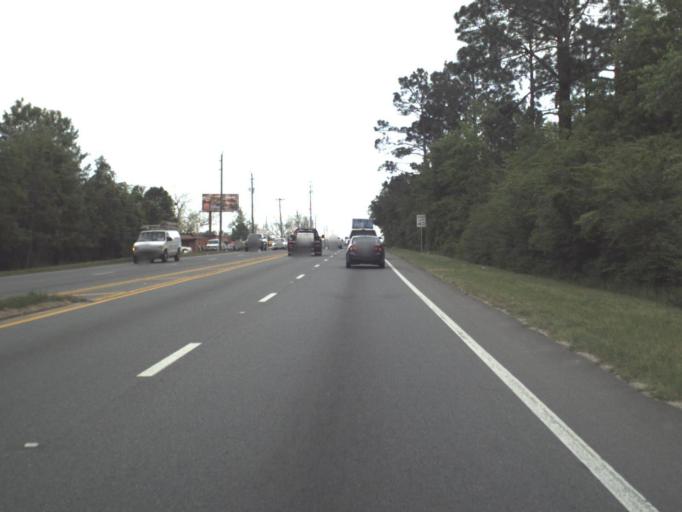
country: US
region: Florida
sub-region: Escambia County
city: Cantonment
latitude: 30.6143
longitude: -87.3224
